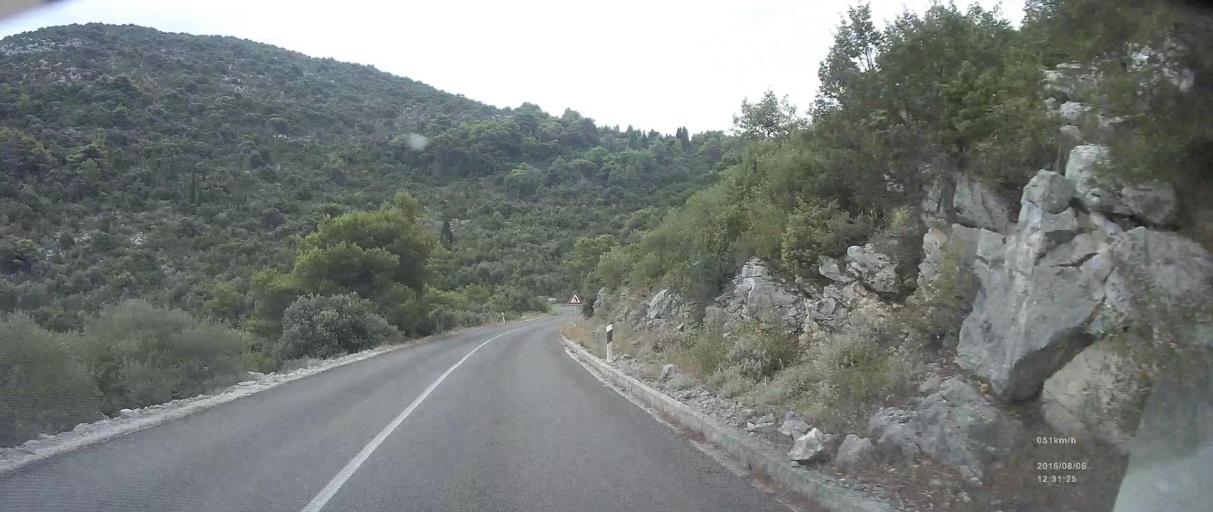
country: HR
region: Dubrovacko-Neretvanska
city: Ston
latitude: 42.7098
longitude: 17.7056
